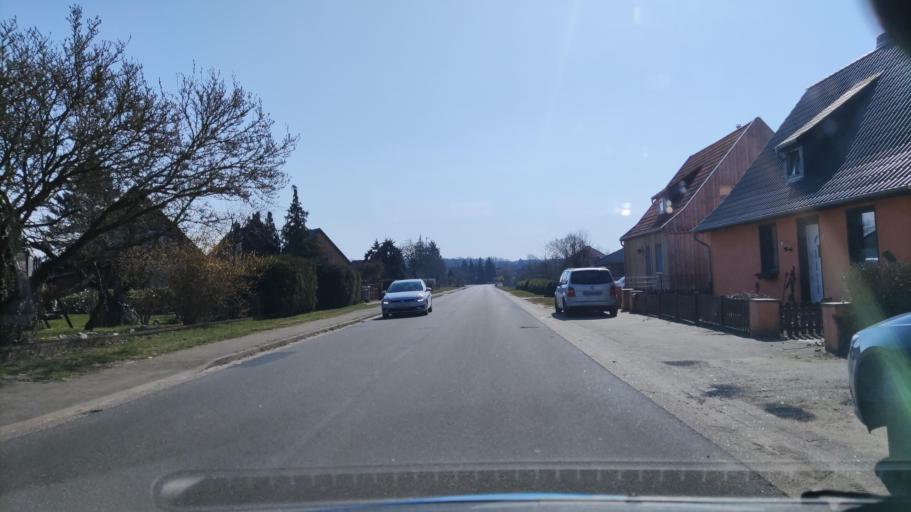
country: DE
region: Lower Saxony
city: Clenze
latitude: 52.9425
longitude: 10.9530
